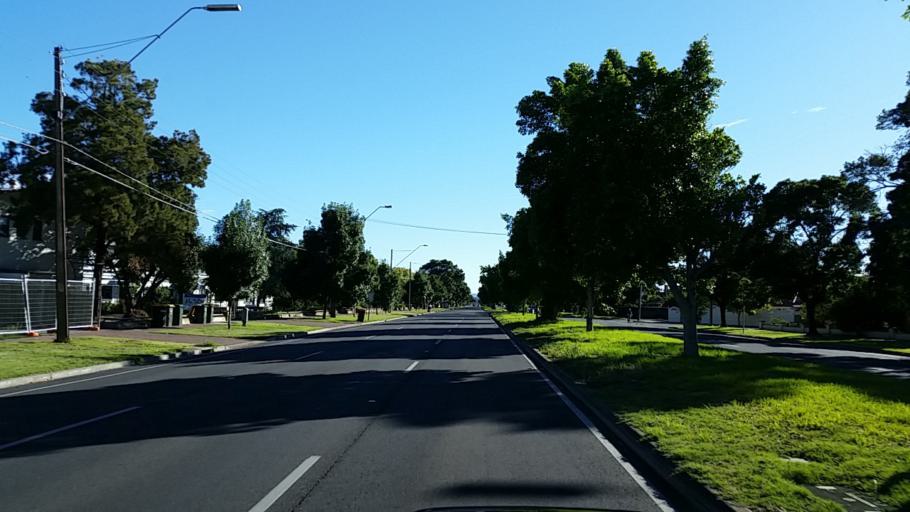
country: AU
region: South Australia
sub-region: Marion
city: Plympton Park
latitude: -34.9719
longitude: 138.5425
